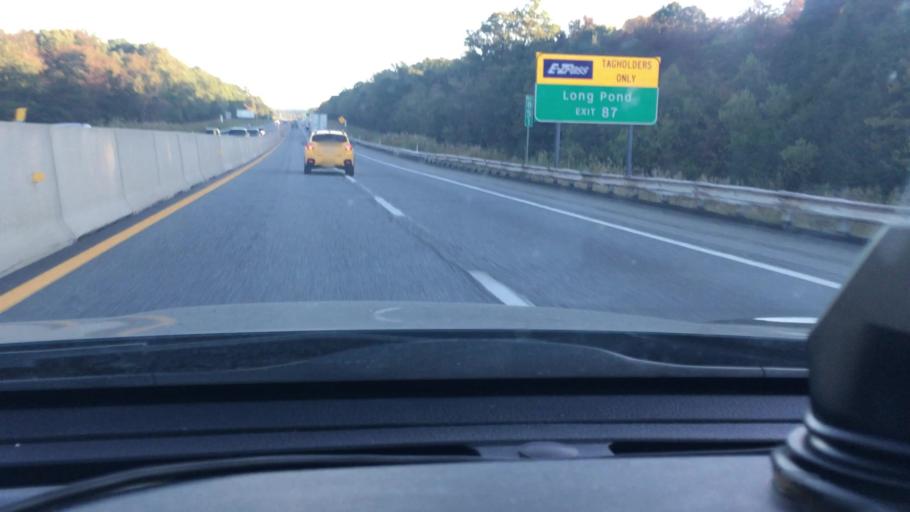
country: US
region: Pennsylvania
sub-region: Carbon County
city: Towamensing Trails
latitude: 40.9551
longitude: -75.6334
